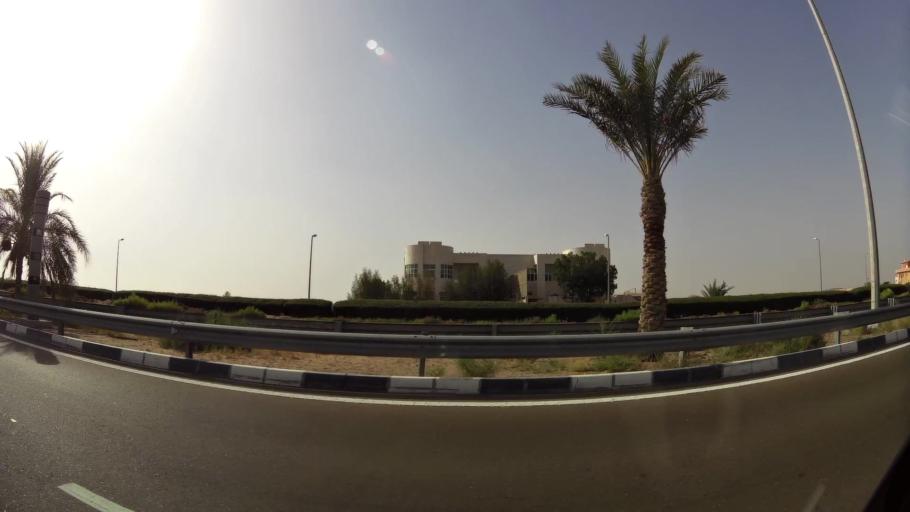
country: AE
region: Abu Dhabi
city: Al Ain
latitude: 24.2221
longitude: 55.6487
